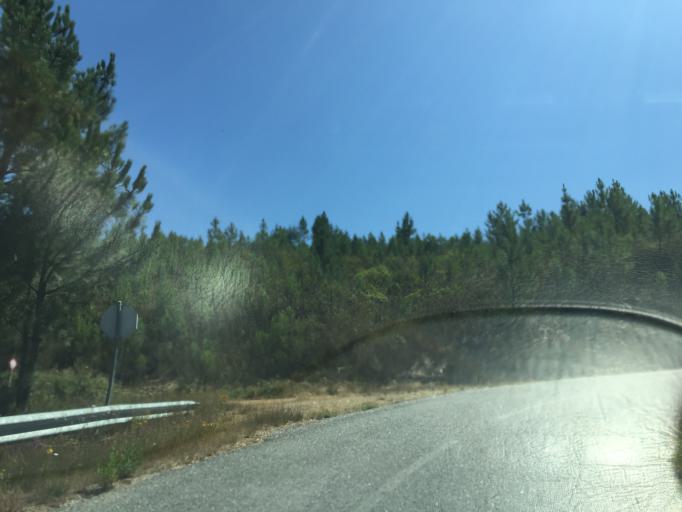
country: PT
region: Coimbra
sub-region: Pampilhosa da Serra
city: Pampilhosa da Serra
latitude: 40.0840
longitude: -7.8260
